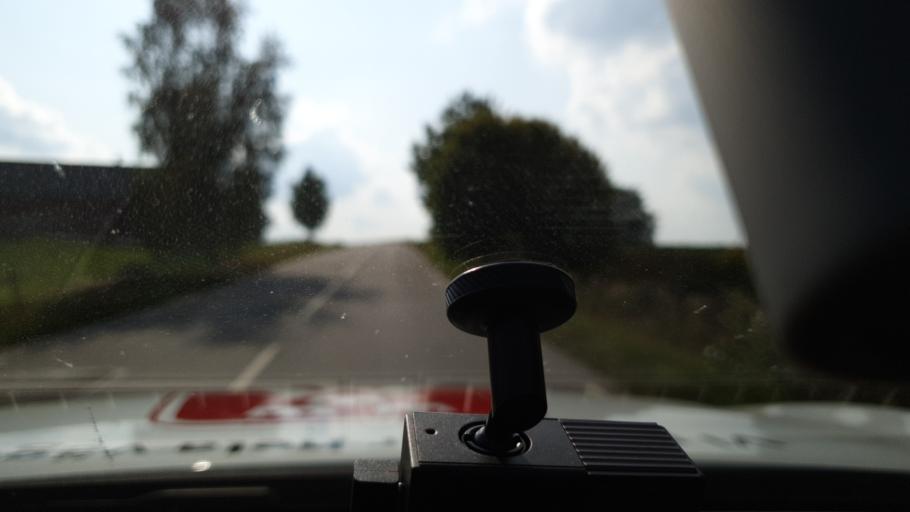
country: SE
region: Kalmar
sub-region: Vimmerby Kommun
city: Sodra Vi
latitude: 57.7175
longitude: 15.8375
